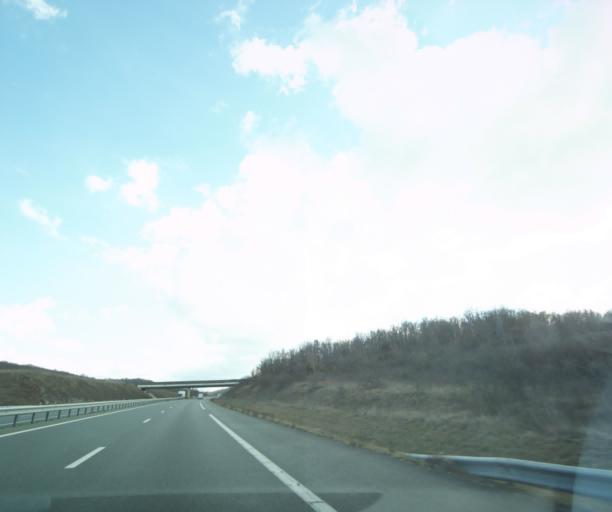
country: FR
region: Midi-Pyrenees
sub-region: Departement du Lot
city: Le Vigan
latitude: 44.7753
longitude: 1.5360
